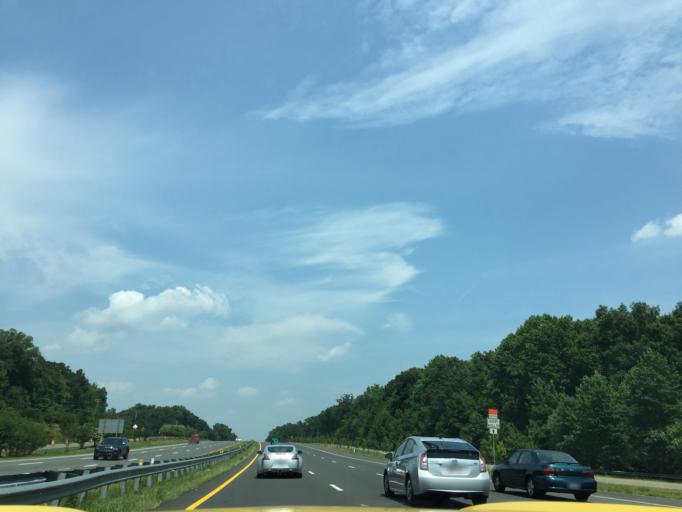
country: US
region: Maryland
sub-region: Prince George's County
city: Accokeek
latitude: 38.6727
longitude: -77.0088
